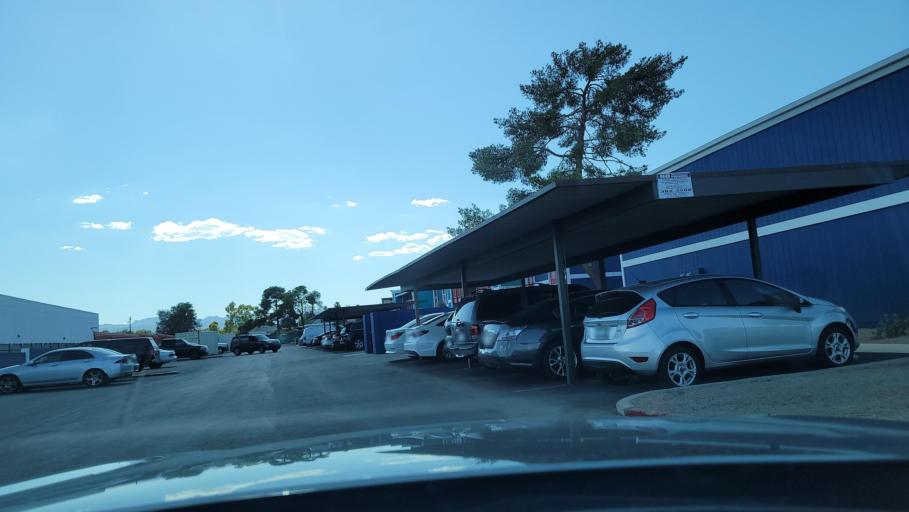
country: US
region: Nevada
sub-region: Clark County
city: Spring Valley
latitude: 36.1283
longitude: -115.1992
